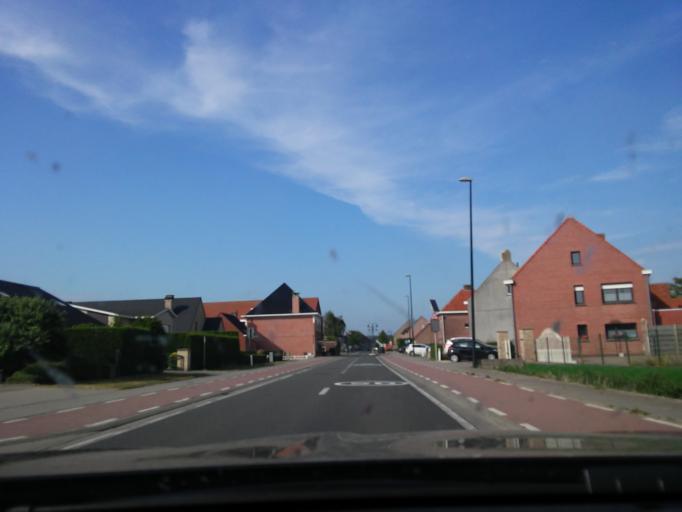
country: BE
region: Flanders
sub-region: Provincie Oost-Vlaanderen
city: Kaprijke
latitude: 51.2440
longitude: 3.6000
